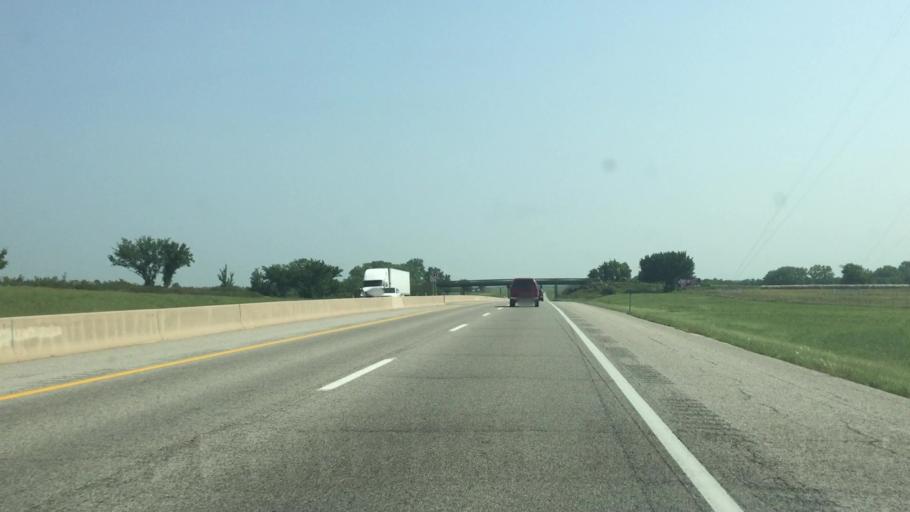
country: US
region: Kansas
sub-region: Lyon County
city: Emporia
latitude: 38.3338
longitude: -96.3028
